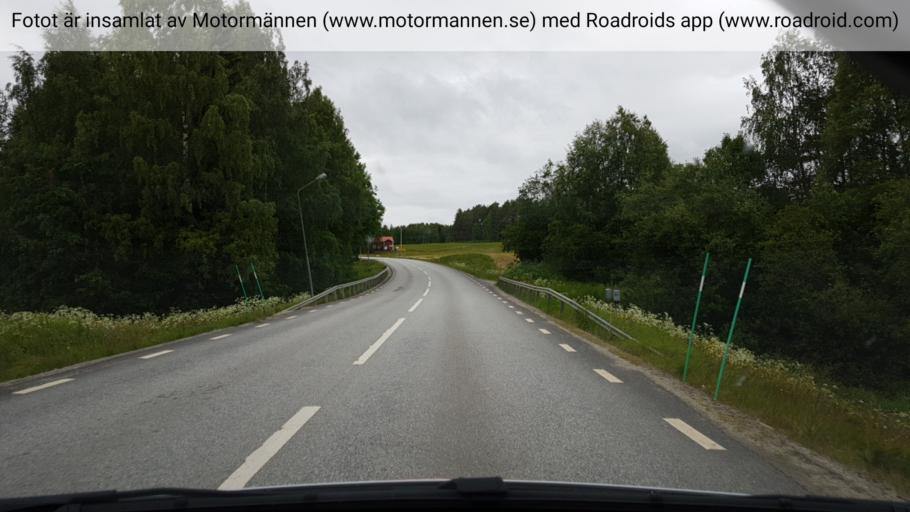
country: SE
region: Vaesterbotten
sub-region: Vindelns Kommun
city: Vindeln
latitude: 64.1256
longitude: 19.5525
